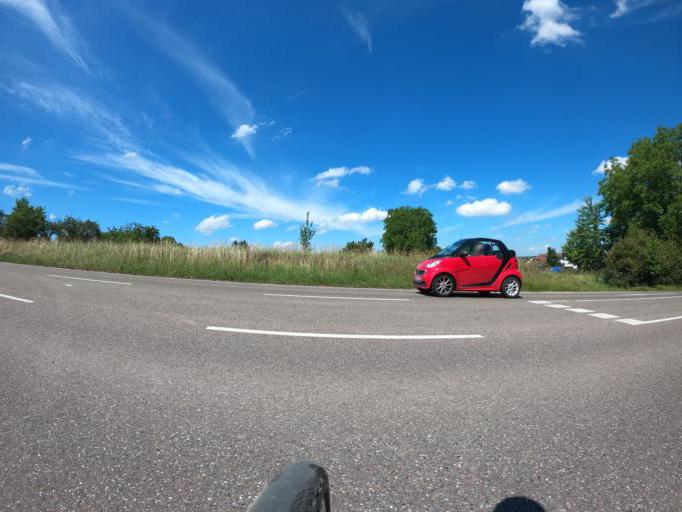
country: DE
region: Baden-Wuerttemberg
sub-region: Regierungsbezirk Stuttgart
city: Asperg
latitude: 48.8991
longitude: 9.1292
